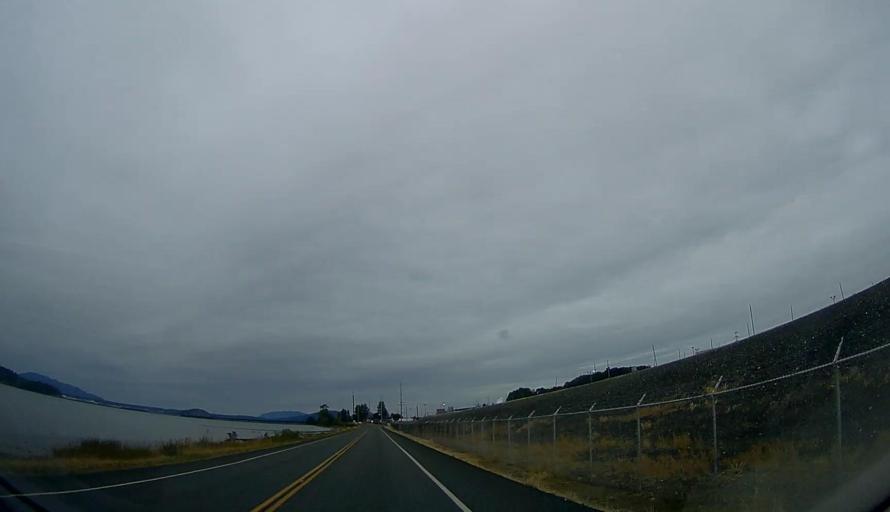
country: US
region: Washington
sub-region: Skagit County
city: Anacortes
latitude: 48.4686
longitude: -122.5690
